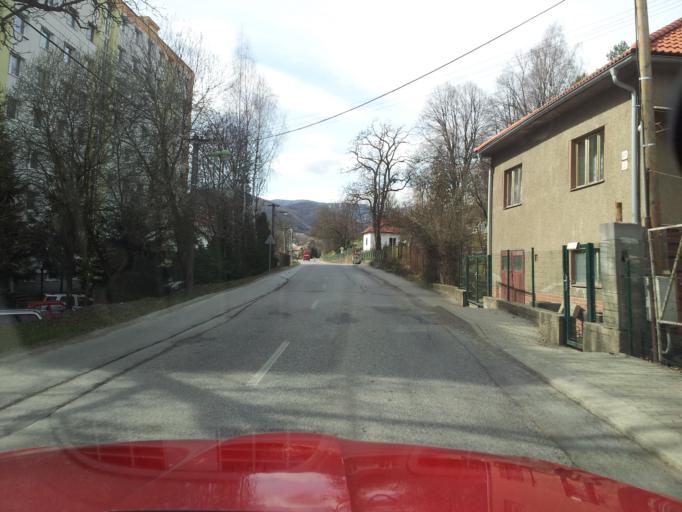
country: SK
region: Banskobystricky
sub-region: Okres Banska Bystrica
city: Banska Bystrica
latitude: 48.7440
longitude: 19.1084
